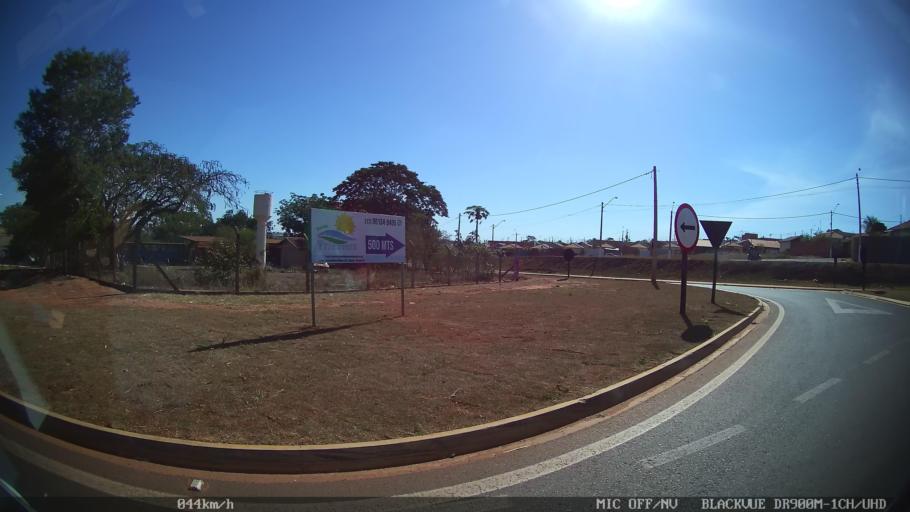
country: BR
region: Sao Paulo
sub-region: Olimpia
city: Olimpia
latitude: -20.7350
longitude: -48.8761
